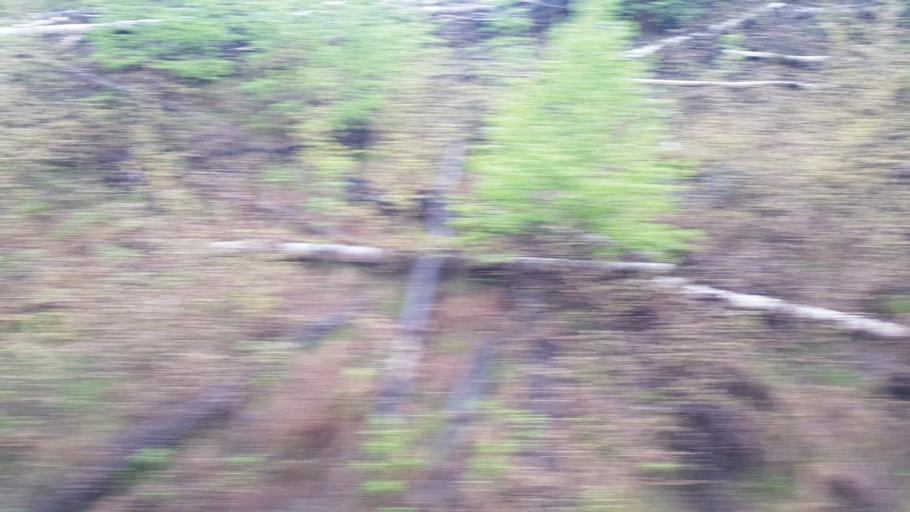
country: NO
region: Oppland
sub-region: Sor-Fron
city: Hundorp
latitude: 61.5565
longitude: 9.9413
